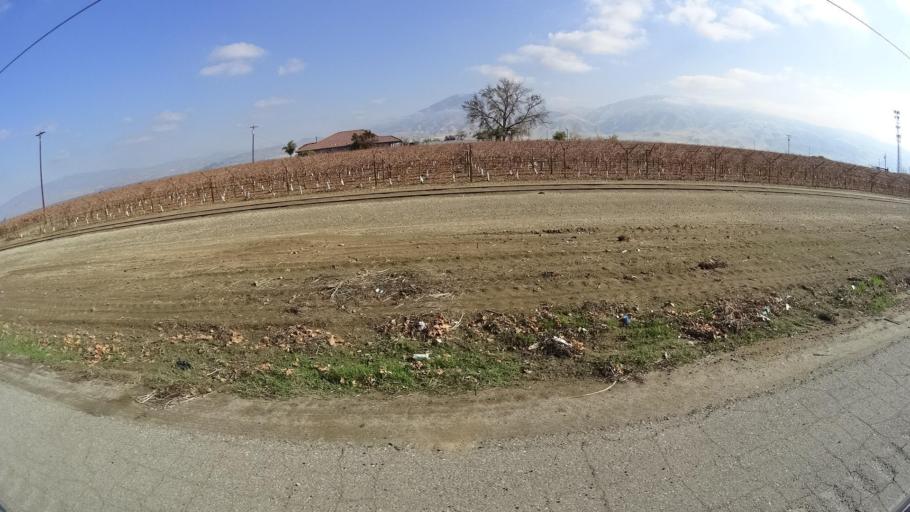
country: US
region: California
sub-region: Kern County
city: Arvin
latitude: 35.2158
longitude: -118.8245
